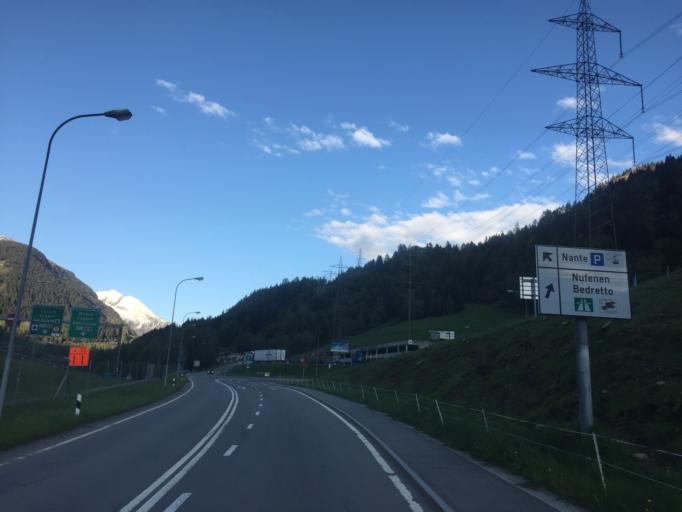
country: CH
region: Ticino
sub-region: Leventina District
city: Airolo
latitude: 46.5250
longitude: 8.6013
